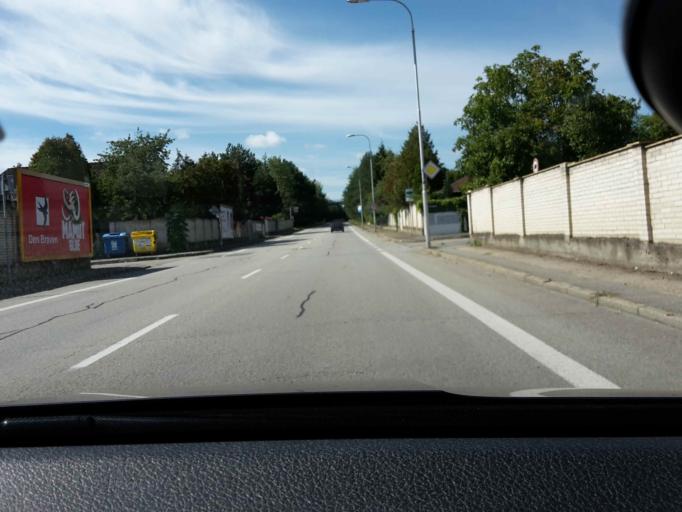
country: CZ
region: Jihocesky
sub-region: Okres Jindrichuv Hradec
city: Jindrichuv Hradec
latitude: 49.1539
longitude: 14.9963
